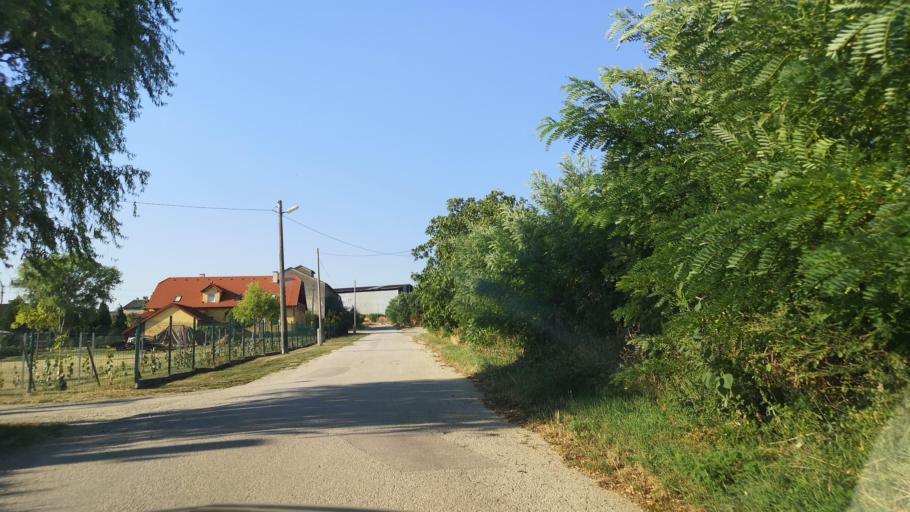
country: SK
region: Nitriansky
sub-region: Okres Nitra
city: Nitra
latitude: 48.3447
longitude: 17.9512
